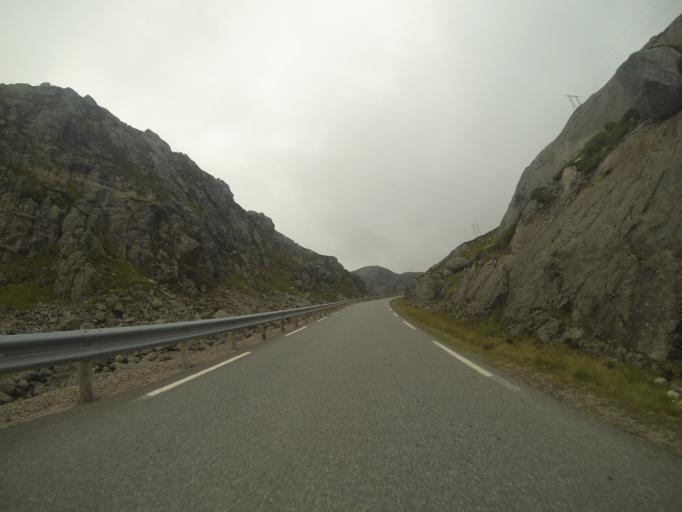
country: NO
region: Vest-Agder
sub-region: Sirdal
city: Tonstad
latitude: 59.0312
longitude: 6.6567
